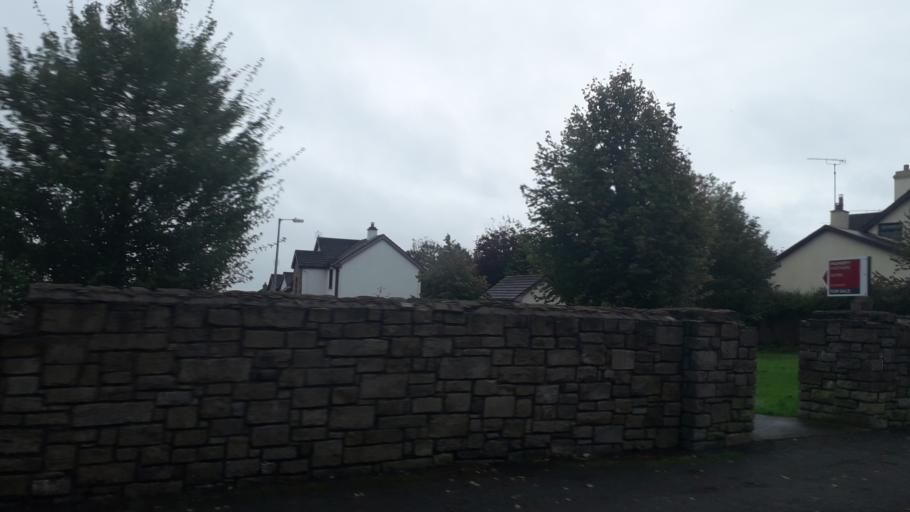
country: IE
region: Leinster
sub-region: An Longfort
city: Longford
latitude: 53.7394
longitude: -7.8021
